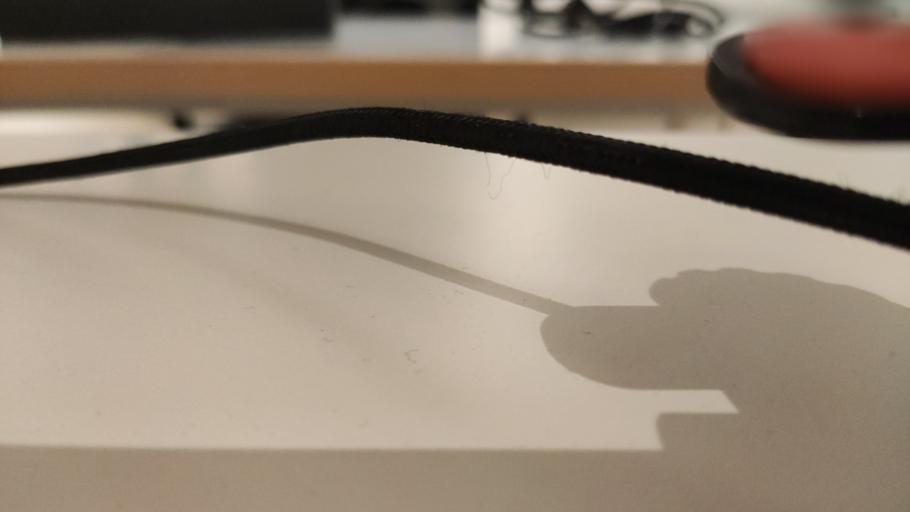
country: RU
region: Moskovskaya
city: Dorokhovo
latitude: 55.4072
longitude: 36.3752
